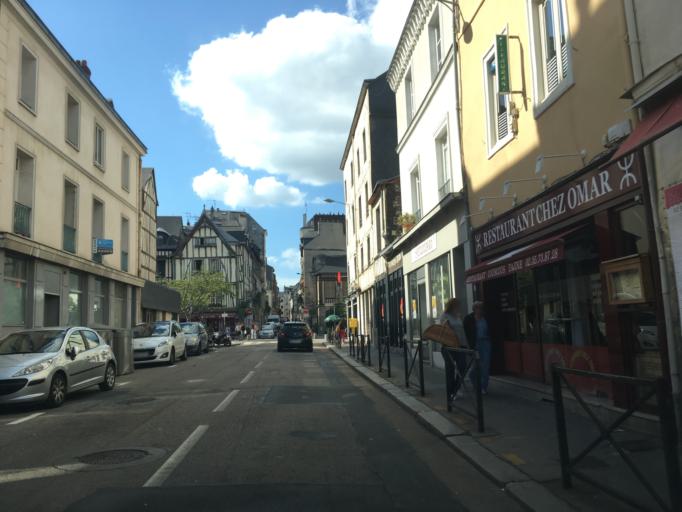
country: FR
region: Haute-Normandie
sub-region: Departement de la Seine-Maritime
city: Rouen
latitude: 49.4411
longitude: 1.0995
